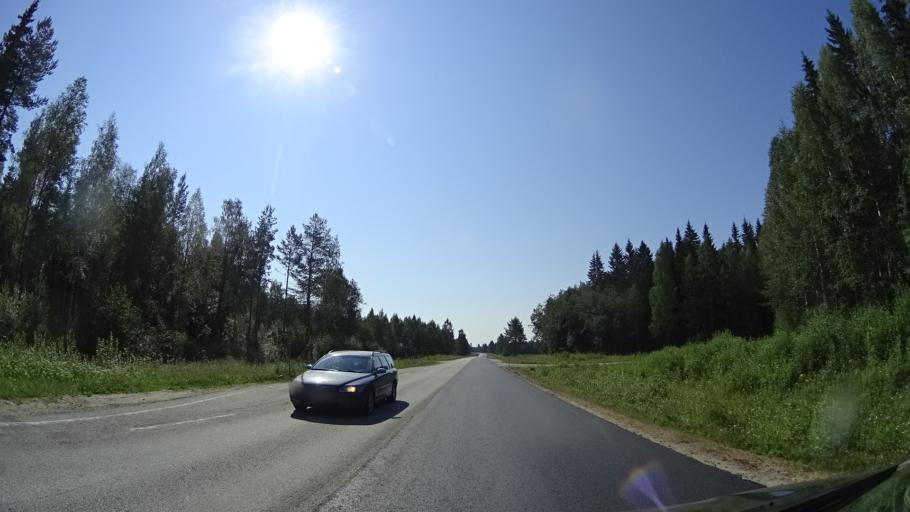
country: FI
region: North Karelia
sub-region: Joensuu
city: Juuka
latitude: 63.2180
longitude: 29.3014
